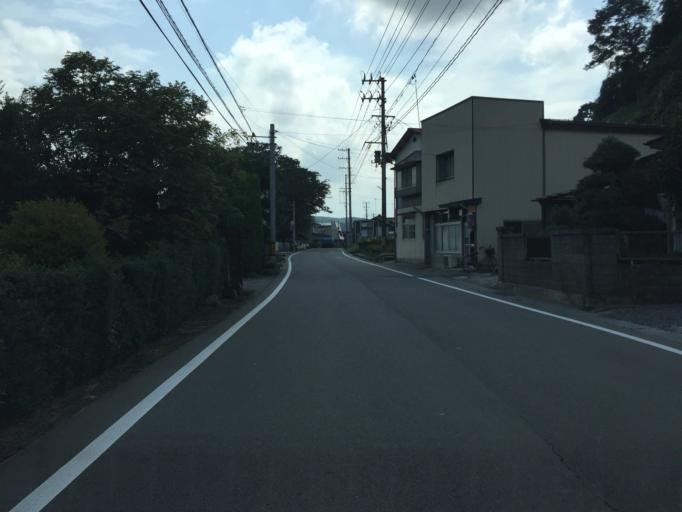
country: JP
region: Fukushima
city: Motomiya
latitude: 37.5229
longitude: 140.4046
